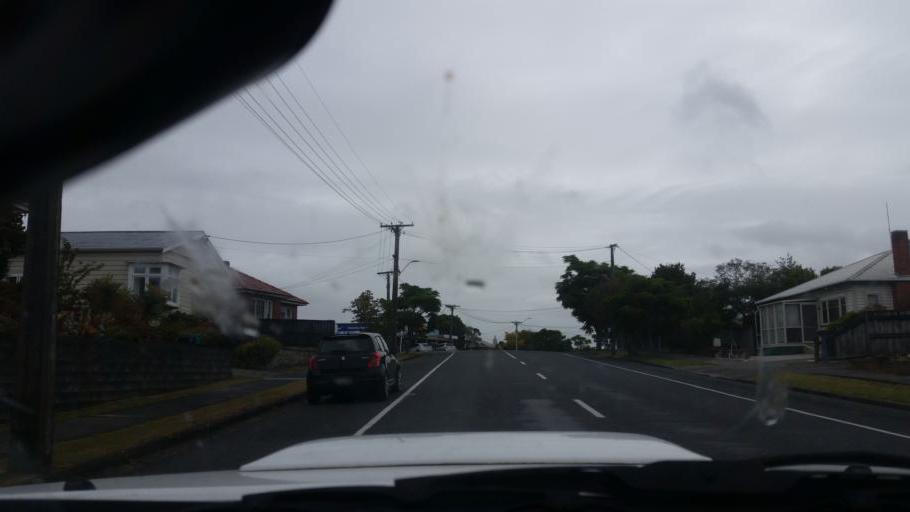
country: NZ
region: Northland
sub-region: Kaipara District
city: Dargaville
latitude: -35.9382
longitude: 173.8741
